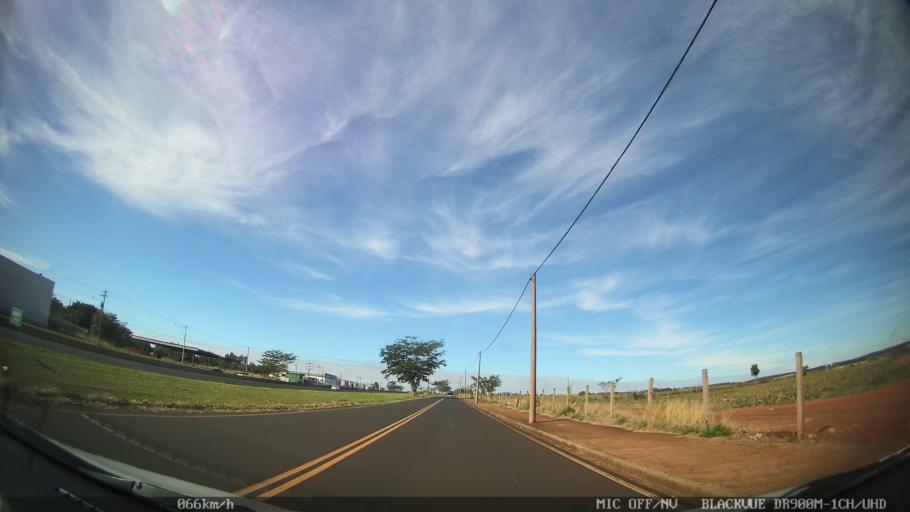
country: BR
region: Sao Paulo
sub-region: Sao Jose Do Rio Preto
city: Sao Jose do Rio Preto
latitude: -20.7937
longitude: -49.3075
